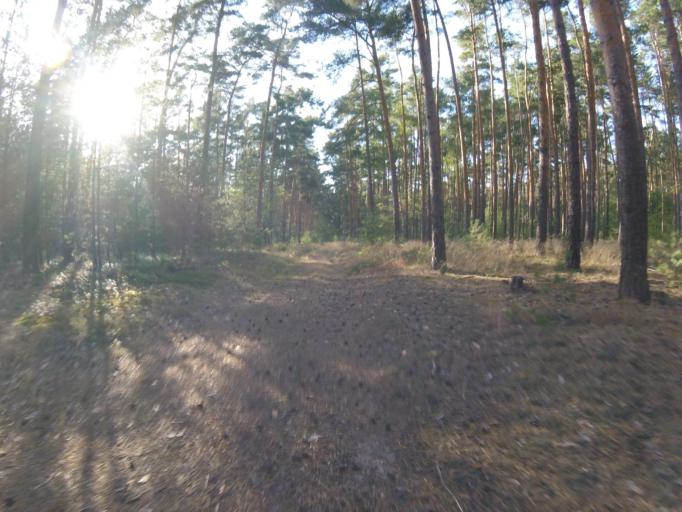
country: DE
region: Brandenburg
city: Wildau
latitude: 52.3347
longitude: 13.6794
